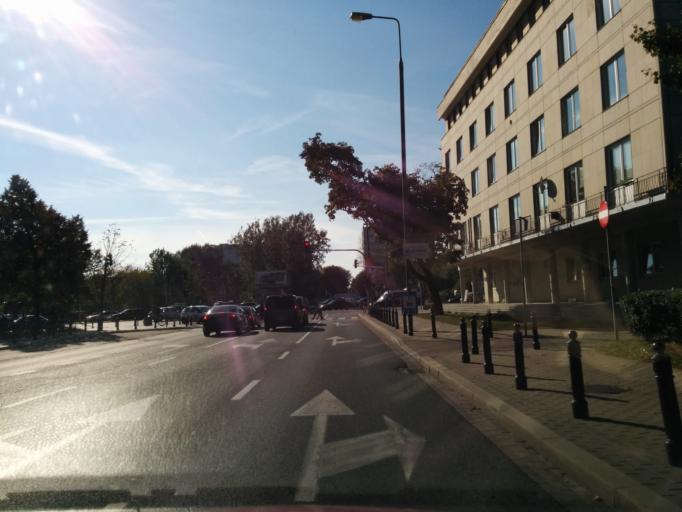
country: PL
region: Masovian Voivodeship
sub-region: Warszawa
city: Srodmiescie
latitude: 52.2131
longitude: 21.0191
